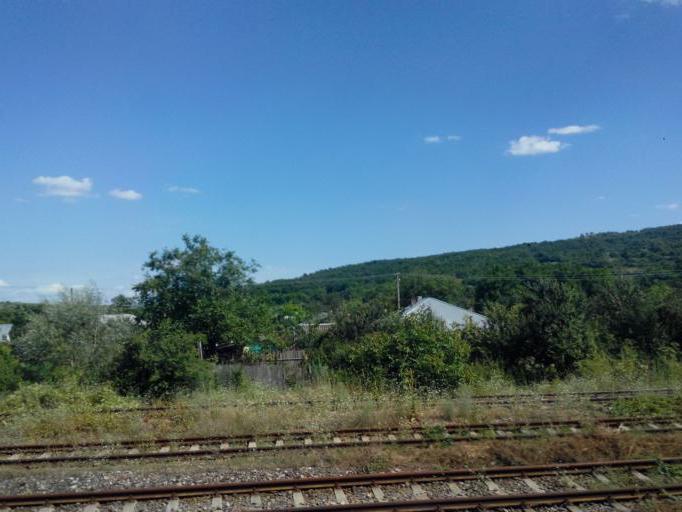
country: RO
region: Vaslui
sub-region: Comuna Zorleni
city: Zorleni
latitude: 46.2690
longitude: 27.7307
